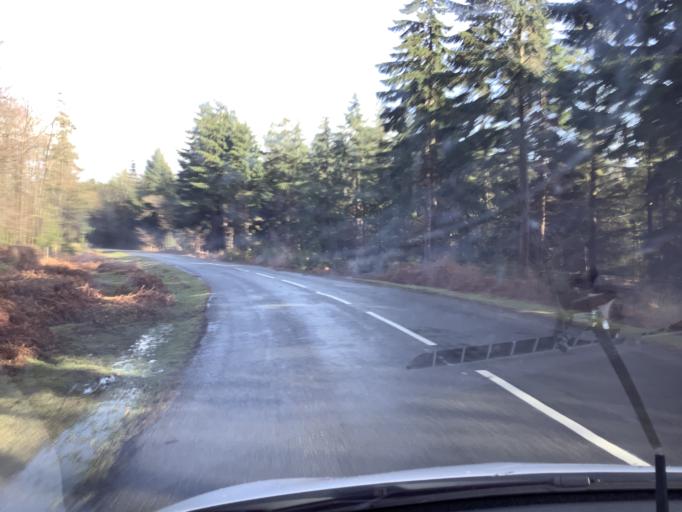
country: GB
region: England
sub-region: Hampshire
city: Brockenhurst
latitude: 50.8190
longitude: -1.5206
